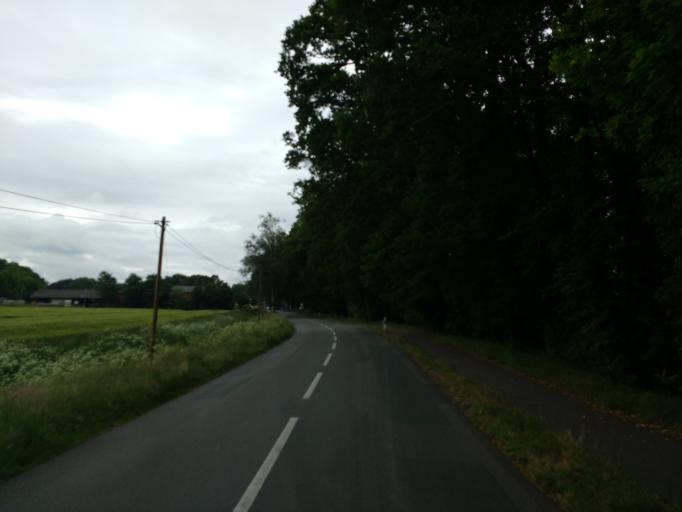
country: DE
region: Lower Saxony
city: Holdorf
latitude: 52.6184
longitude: 8.1463
